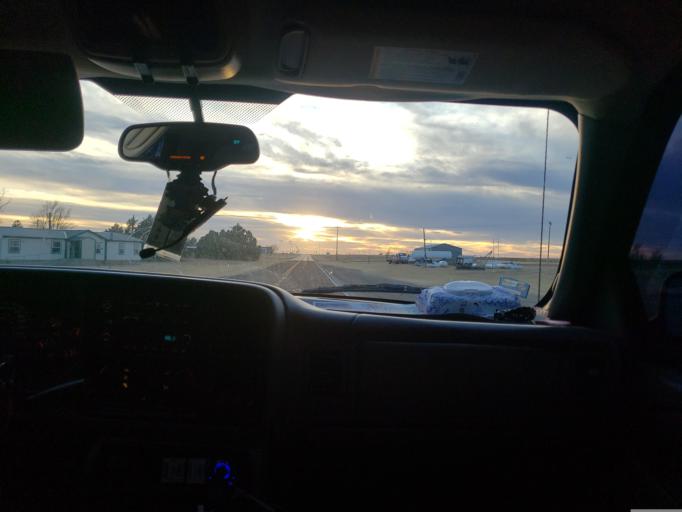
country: US
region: Oklahoma
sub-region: Cimarron County
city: Boise City
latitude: 36.8101
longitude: -102.2553
